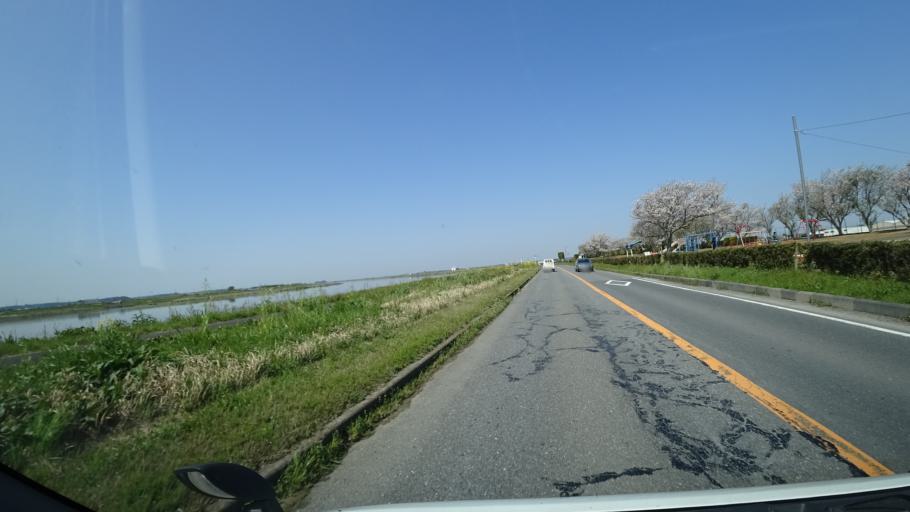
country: JP
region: Chiba
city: Katori-shi
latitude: 35.9184
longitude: 140.4725
